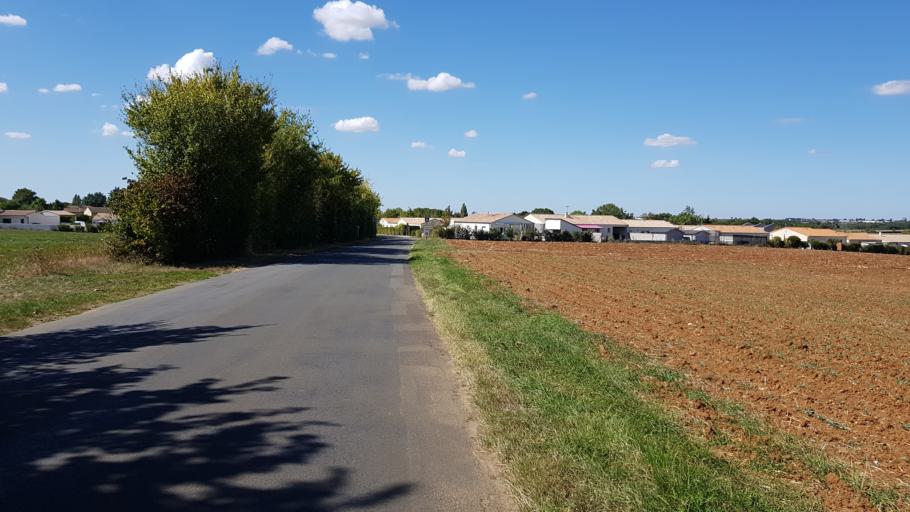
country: FR
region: Poitou-Charentes
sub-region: Departement des Deux-Sevres
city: Vouille
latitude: 46.3135
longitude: -0.3555
